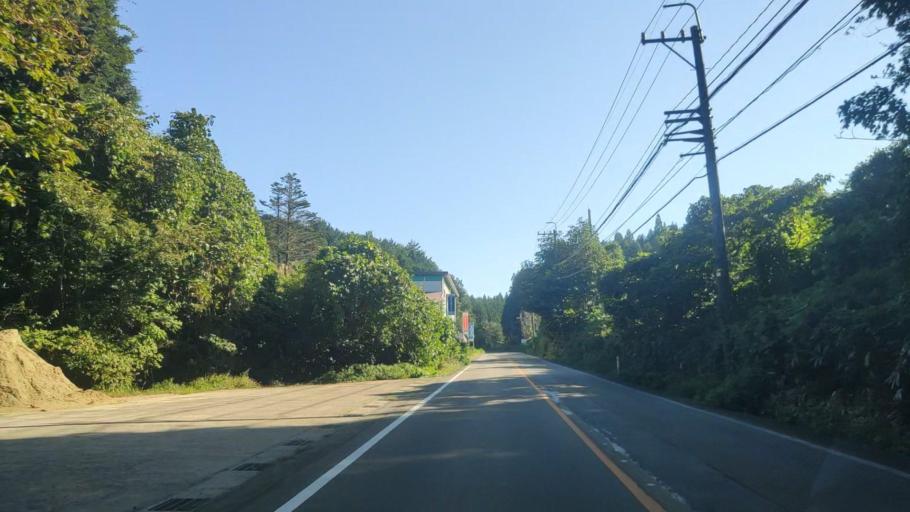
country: JP
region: Ishikawa
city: Nanao
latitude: 37.1357
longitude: 136.8629
